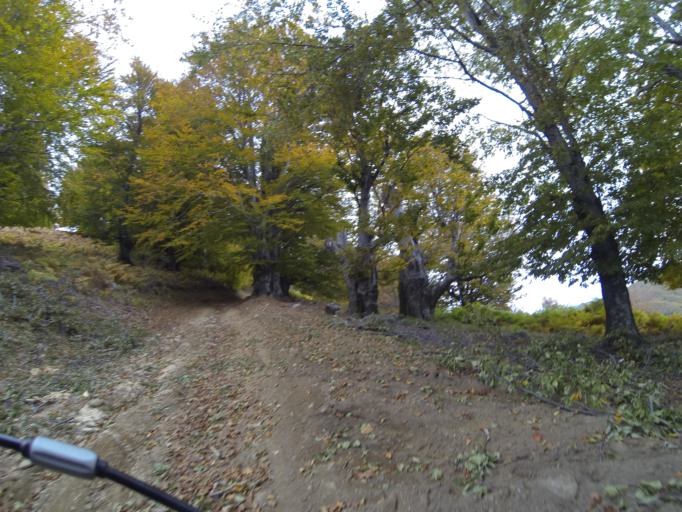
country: RO
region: Gorj
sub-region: Comuna Tismana
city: Sohodol
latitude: 45.1302
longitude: 22.8701
